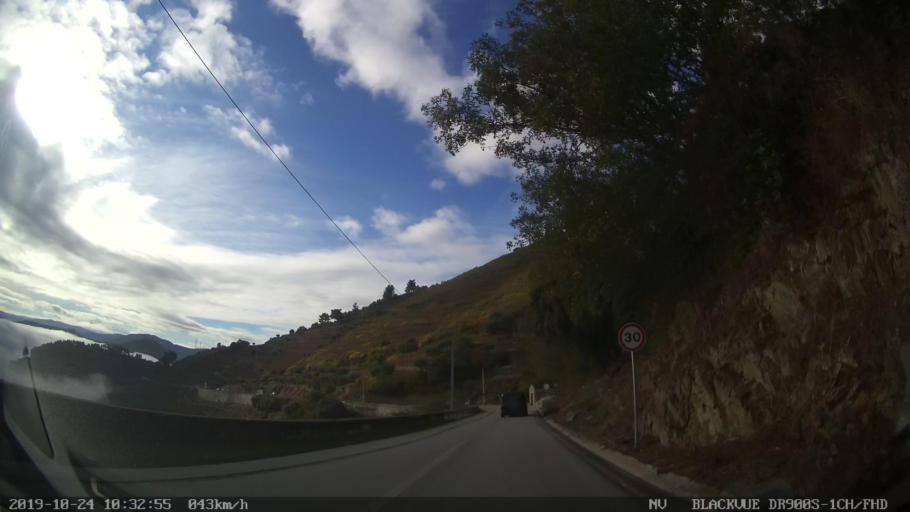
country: PT
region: Vila Real
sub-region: Sabrosa
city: Vilela
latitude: 41.2108
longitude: -7.5551
